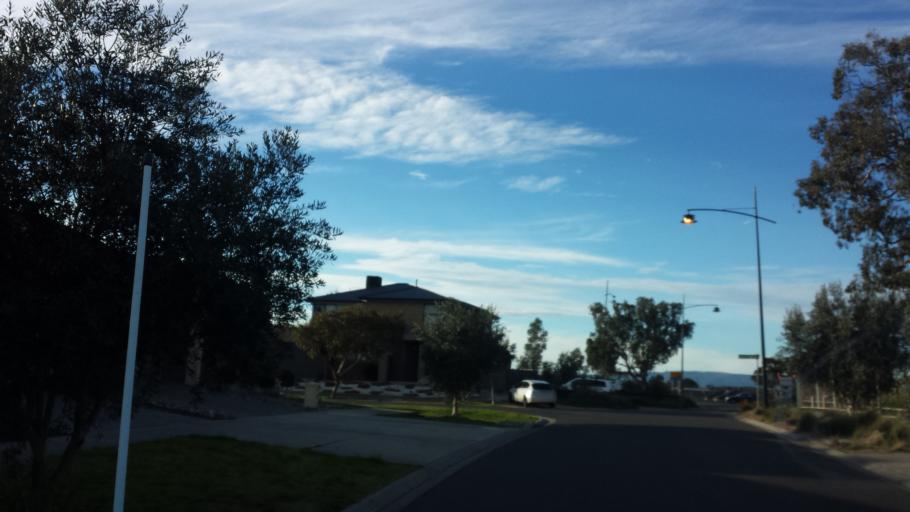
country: AU
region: Victoria
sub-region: Whittlesea
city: Mernda
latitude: -37.6011
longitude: 145.0917
